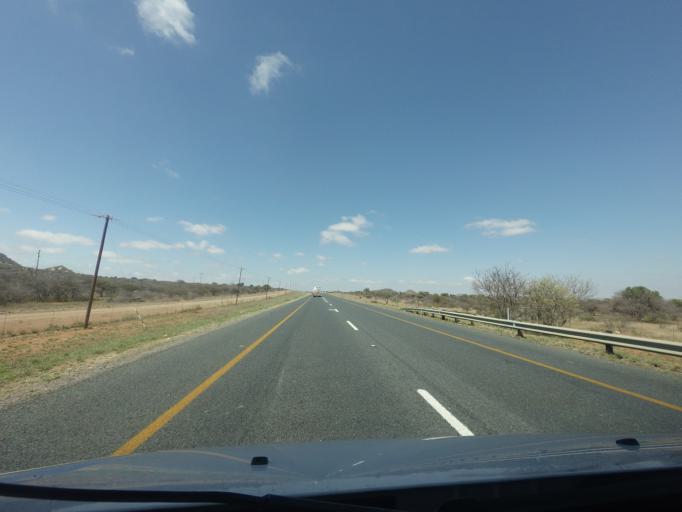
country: ZA
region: Limpopo
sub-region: Vhembe District Municipality
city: Louis Trichardt
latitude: -23.4207
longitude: 29.7516
